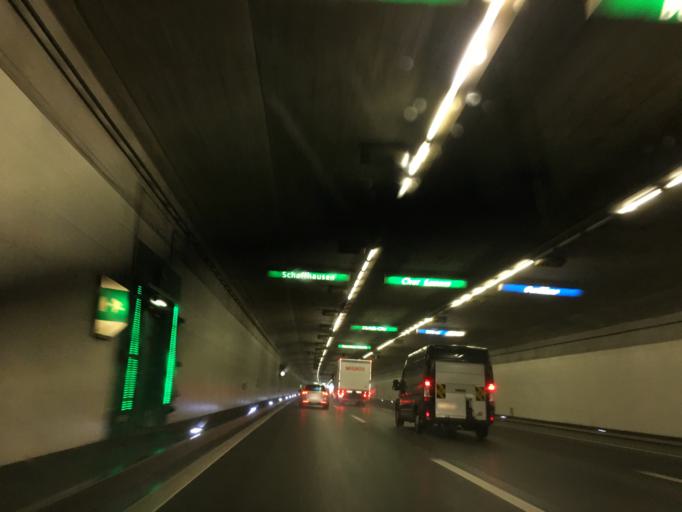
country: CH
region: Zurich
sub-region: Bezirk Buelach
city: Opfikon
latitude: 47.4345
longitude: 8.5712
